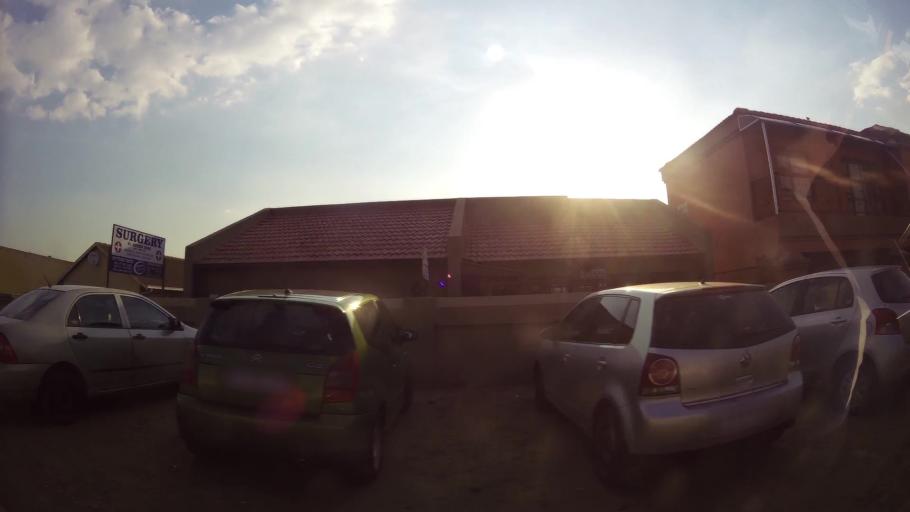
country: ZA
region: Gauteng
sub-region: Ekurhuleni Metropolitan Municipality
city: Germiston
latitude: -26.3476
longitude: 28.2139
